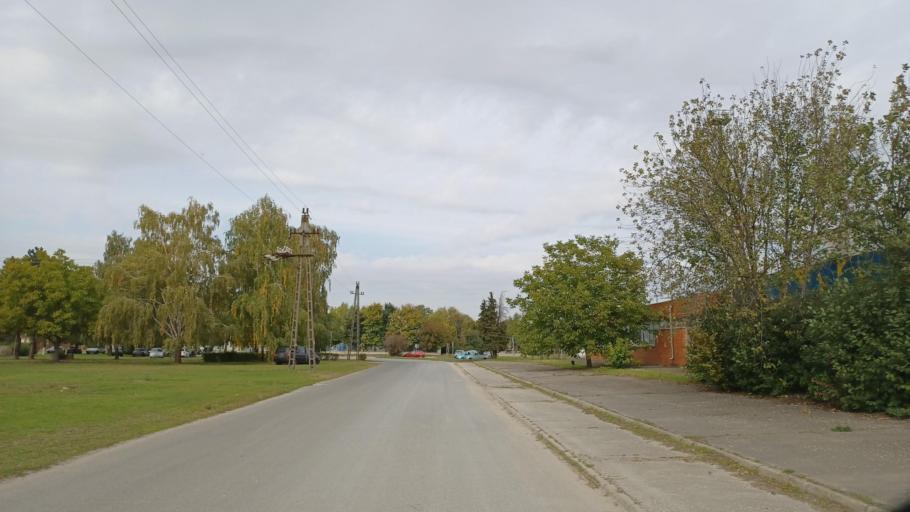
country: HU
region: Tolna
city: Paks
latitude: 46.6065
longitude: 18.8524
